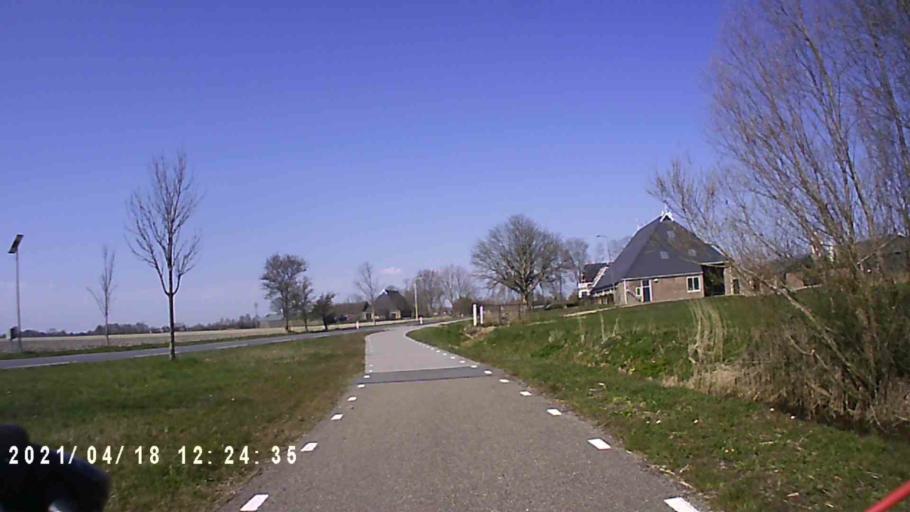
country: NL
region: Friesland
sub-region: Gemeente Dongeradeel
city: Anjum
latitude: 53.3276
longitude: 6.1167
